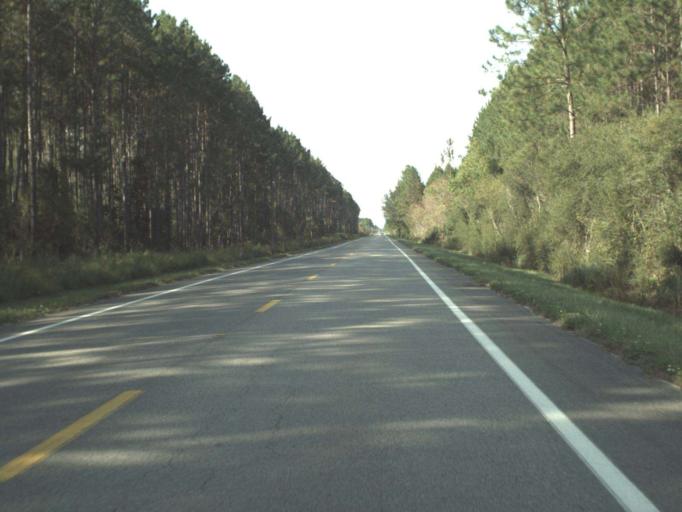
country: US
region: Florida
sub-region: Gulf County
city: Wewahitchka
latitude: 30.0132
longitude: -85.1763
